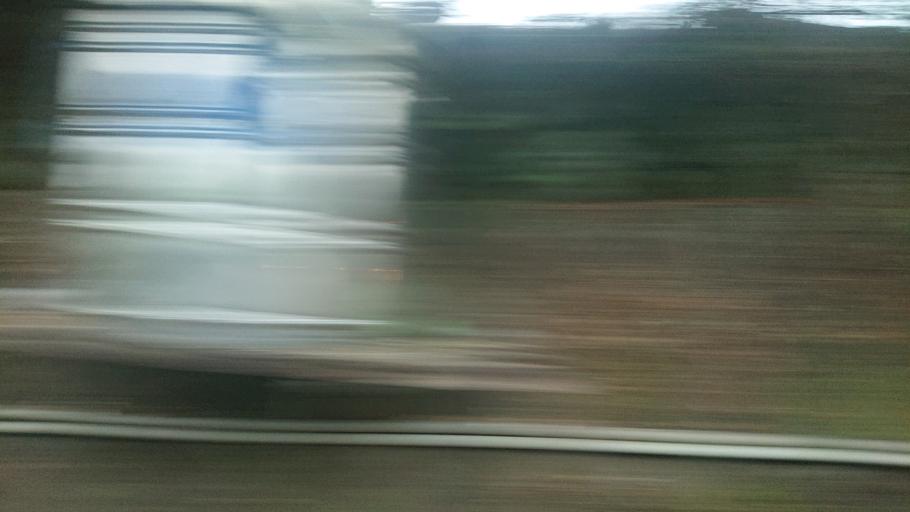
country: TW
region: Taiwan
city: Lugu
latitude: 23.6023
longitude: 120.7078
